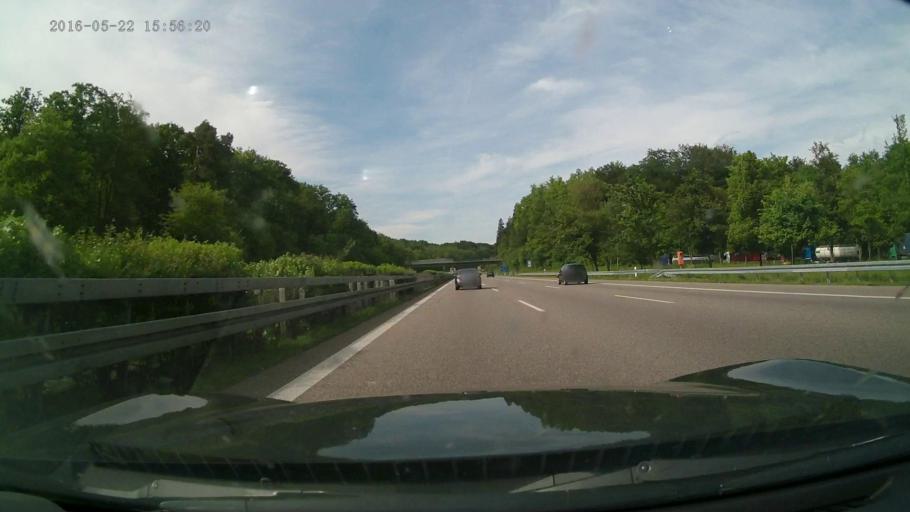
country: DE
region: Baden-Wuerttemberg
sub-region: Regierungsbezirk Stuttgart
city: Untergruppenbach
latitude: 49.0924
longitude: 9.2924
